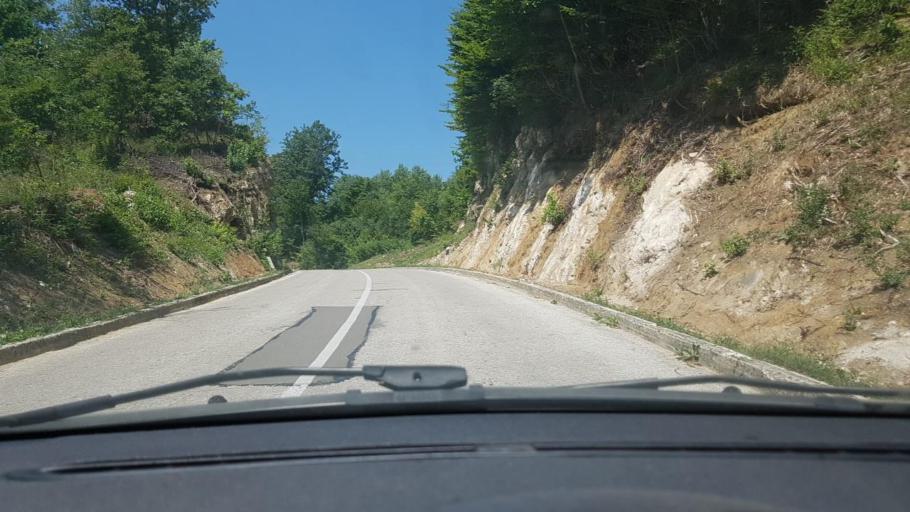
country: BA
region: Federation of Bosnia and Herzegovina
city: Orasac
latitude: 44.5964
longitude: 16.0760
